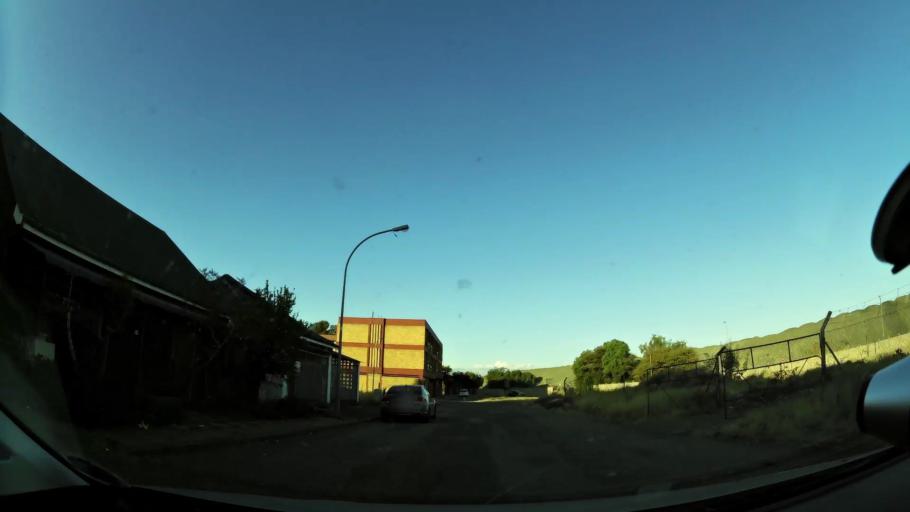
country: ZA
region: Northern Cape
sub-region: Frances Baard District Municipality
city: Kimberley
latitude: -28.7366
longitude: 24.7723
